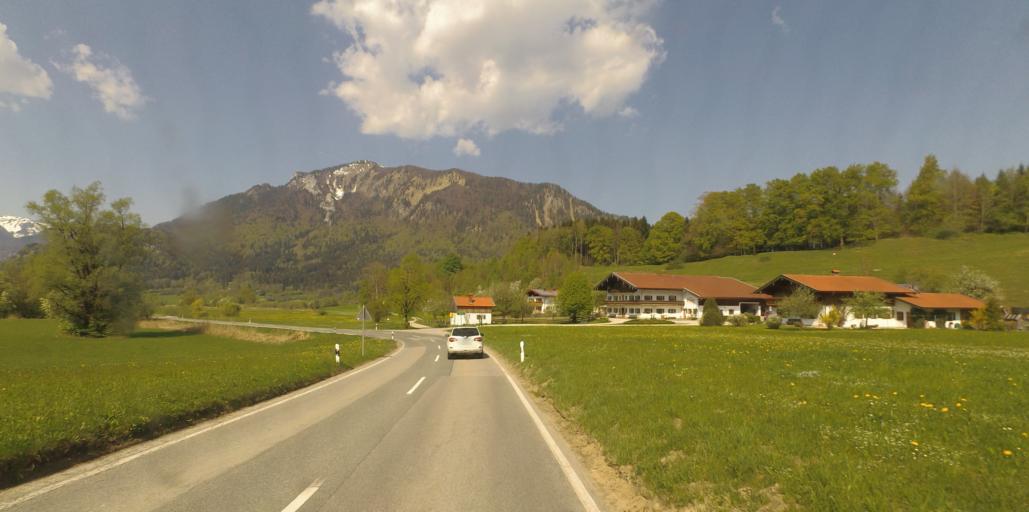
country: DE
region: Bavaria
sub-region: Upper Bavaria
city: Marquartstein
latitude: 47.7444
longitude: 12.4472
